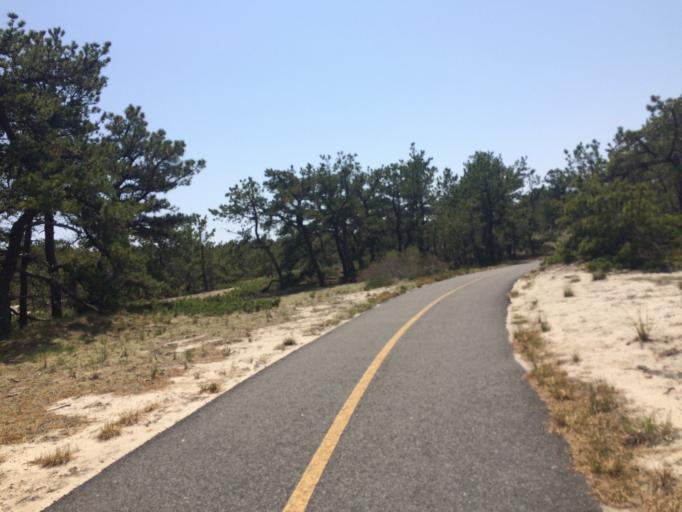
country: US
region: Massachusetts
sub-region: Barnstable County
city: Provincetown
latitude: 42.0661
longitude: -70.2124
